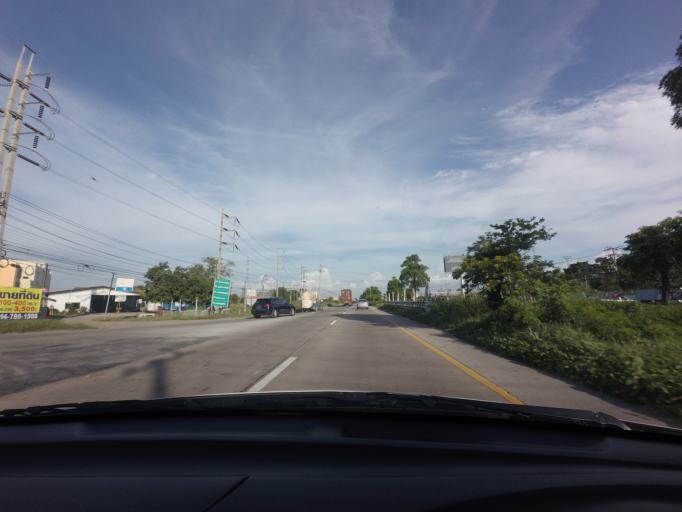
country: TH
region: Phra Nakhon Si Ayutthaya
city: Lat Bua Luang
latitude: 14.0853
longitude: 100.3114
